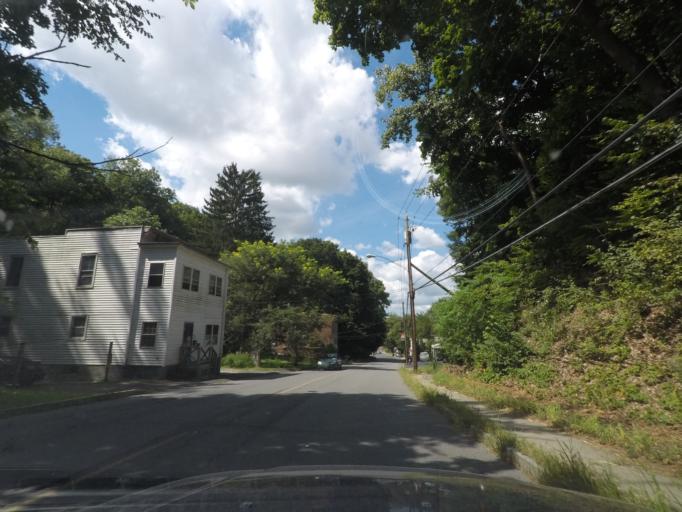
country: US
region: New York
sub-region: Rensselaer County
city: Troy
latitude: 42.7175
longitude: -73.6799
